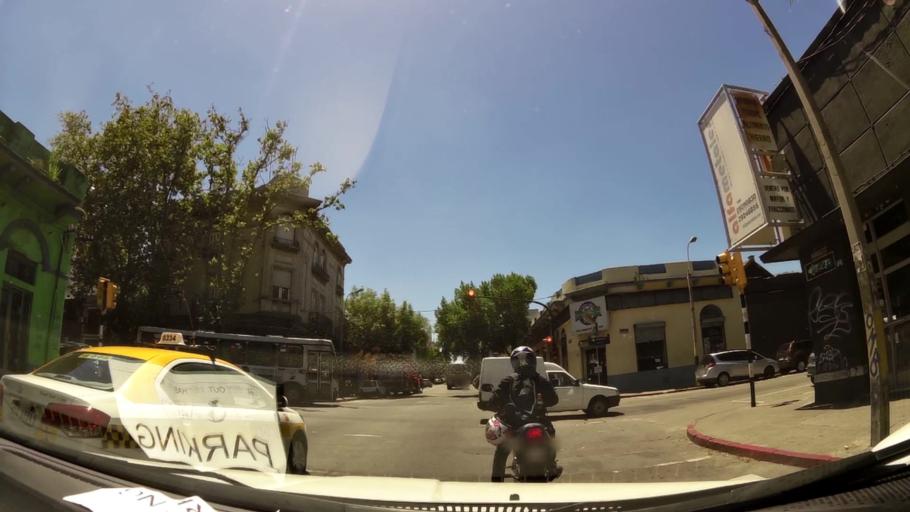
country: UY
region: Montevideo
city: Montevideo
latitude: -34.8967
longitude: -56.1836
